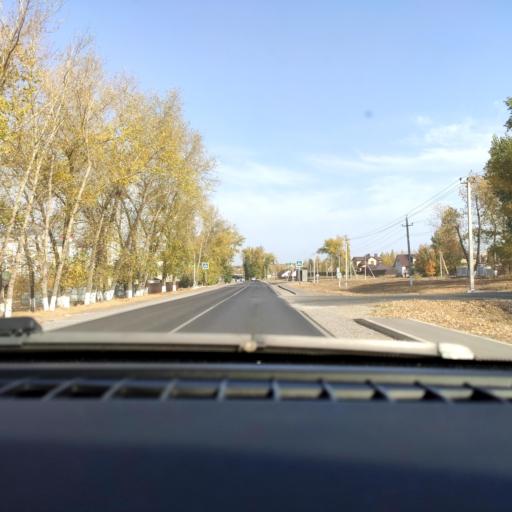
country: RU
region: Voronezj
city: Novaya Usman'
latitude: 51.6653
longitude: 39.4037
